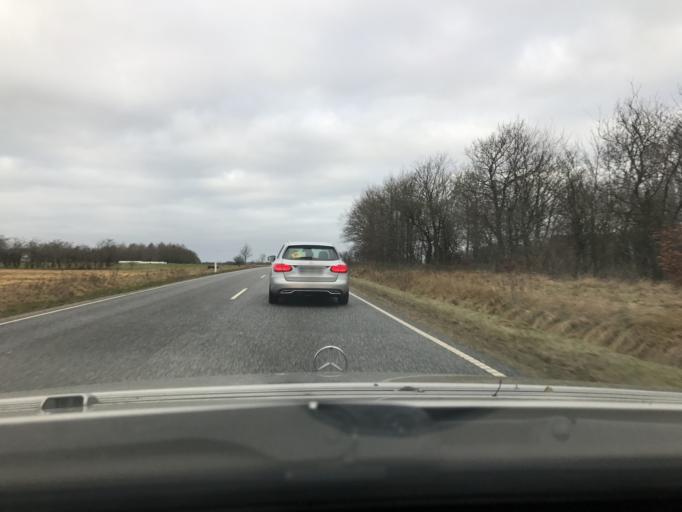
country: DK
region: South Denmark
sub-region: Tonder Kommune
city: Toftlund
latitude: 55.1206
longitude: 9.1550
